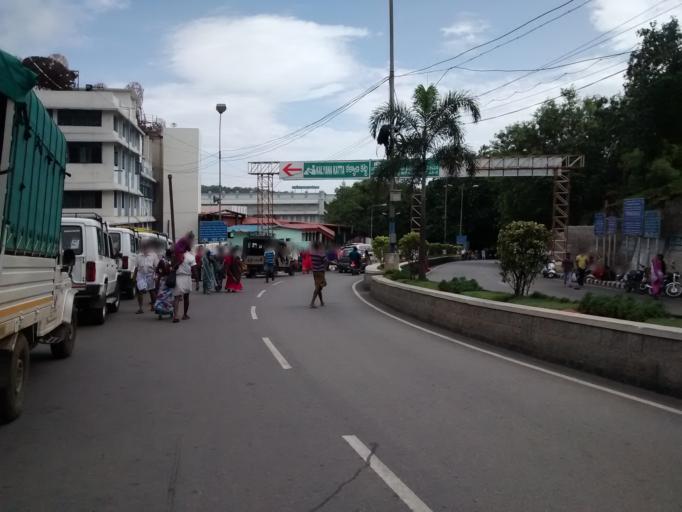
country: IN
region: Andhra Pradesh
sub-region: Chittoor
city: Tirumala
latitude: 13.6817
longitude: 79.3502
